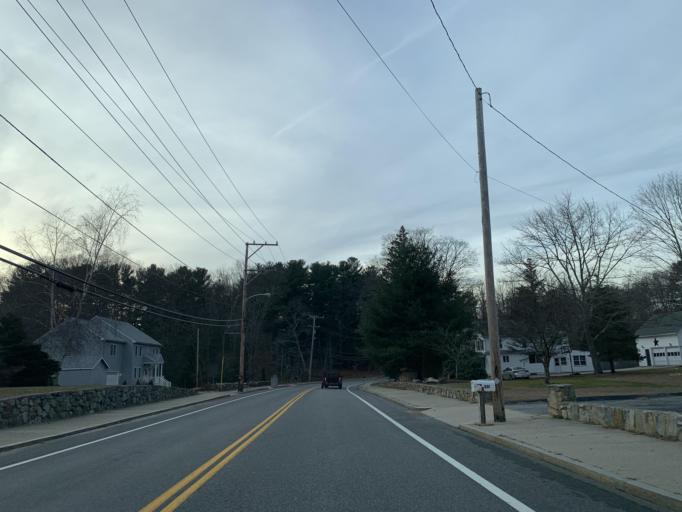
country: US
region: Rhode Island
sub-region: Providence County
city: Greenville
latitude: 41.8613
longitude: -71.5399
